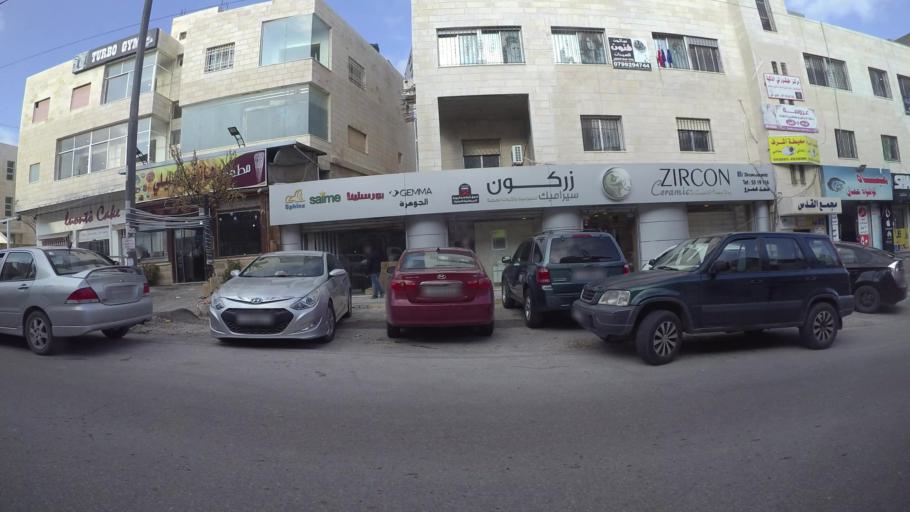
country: JO
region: Amman
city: Al Jubayhah
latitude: 31.9859
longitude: 35.8577
